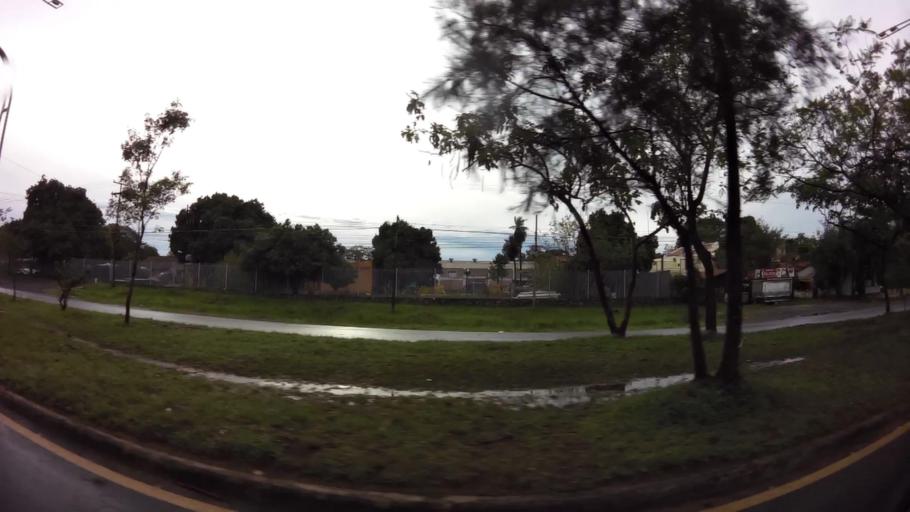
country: PY
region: Central
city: Fernando de la Mora
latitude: -25.2557
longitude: -57.5141
